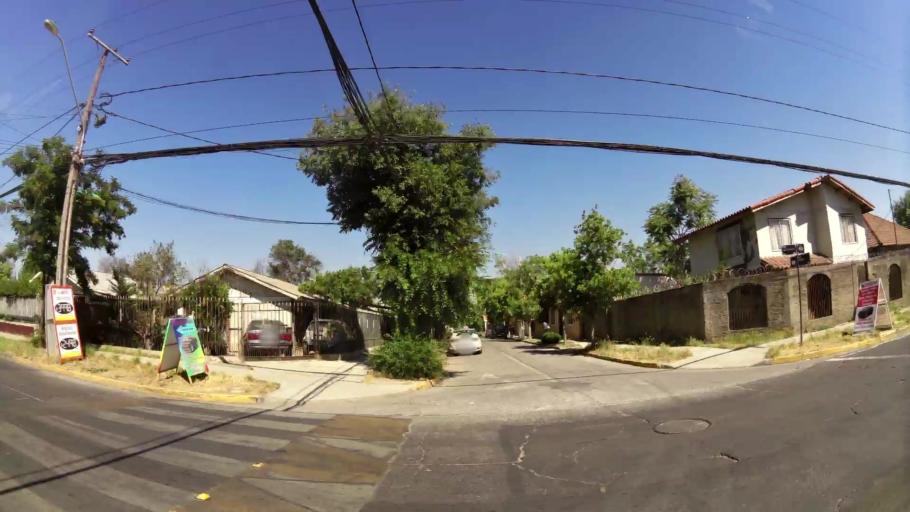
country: CL
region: Santiago Metropolitan
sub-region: Provincia de Santiago
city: La Pintana
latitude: -33.5496
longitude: -70.6597
